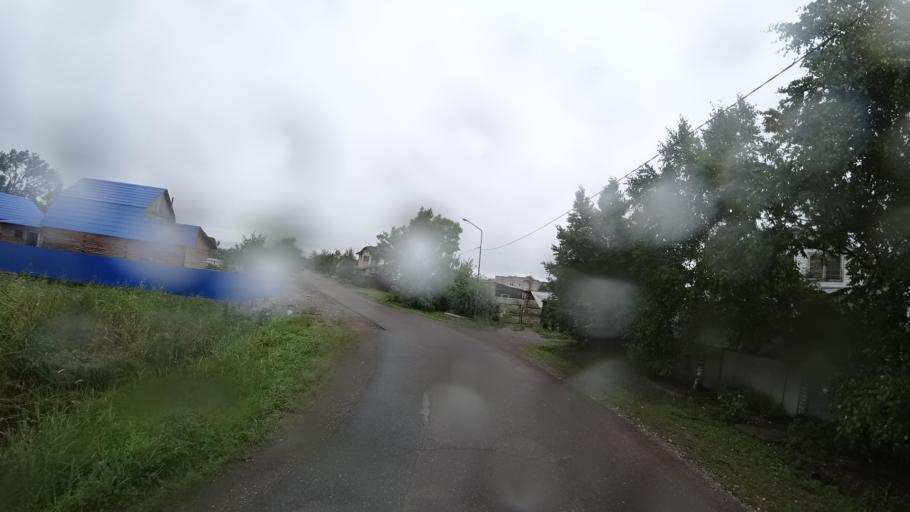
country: RU
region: Primorskiy
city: Monastyrishche
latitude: 44.1988
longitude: 132.4318
